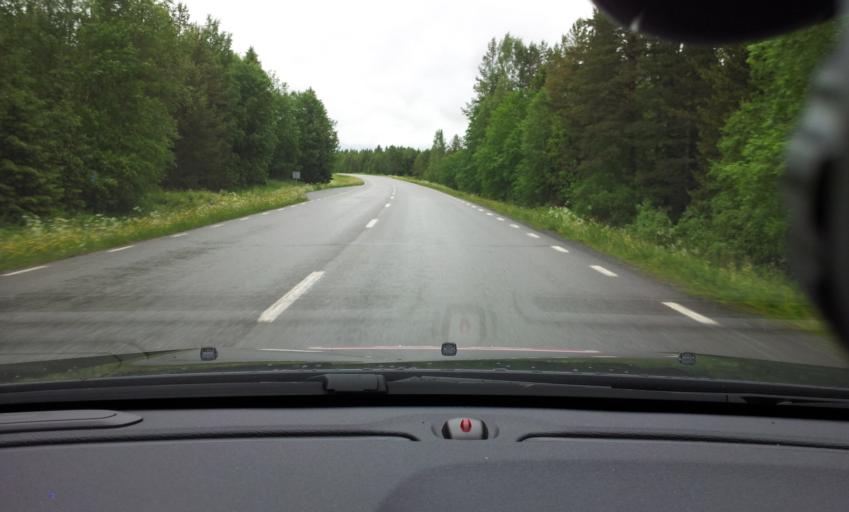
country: SE
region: Jaemtland
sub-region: Krokoms Kommun
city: Krokom
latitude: 63.3664
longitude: 14.5073
